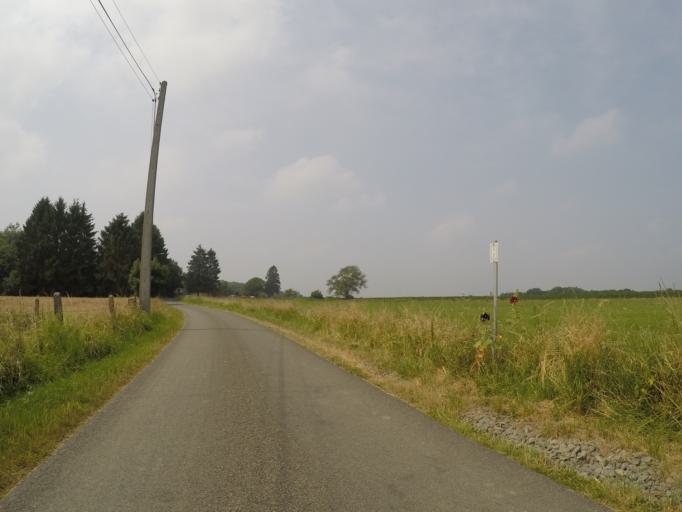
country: BE
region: Wallonia
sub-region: Province de Namur
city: Assesse
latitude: 50.3445
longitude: 4.9896
